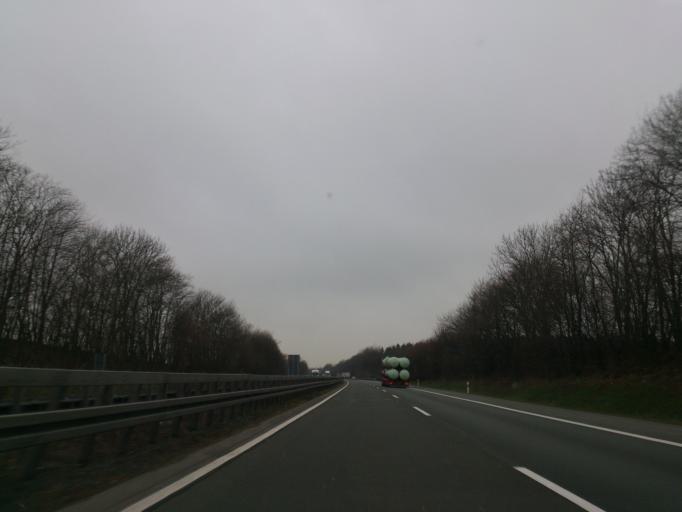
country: DE
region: North Rhine-Westphalia
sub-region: Regierungsbezirk Detmold
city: Wunnenberg
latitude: 51.5870
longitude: 8.7017
